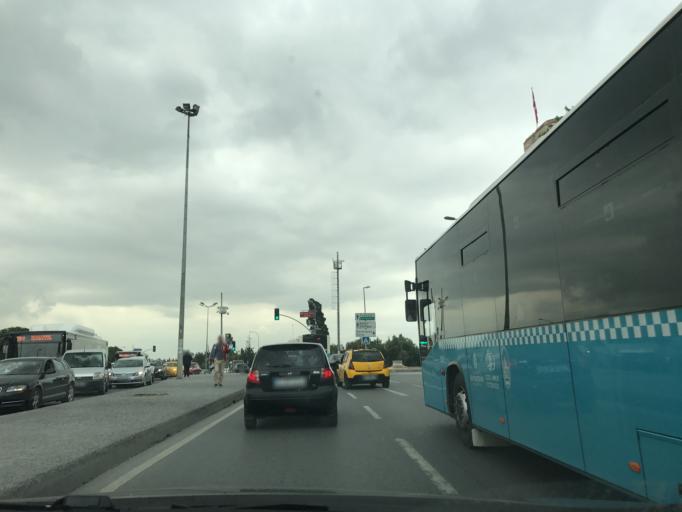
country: TR
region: Istanbul
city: Istanbul
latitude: 41.0308
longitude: 28.9364
